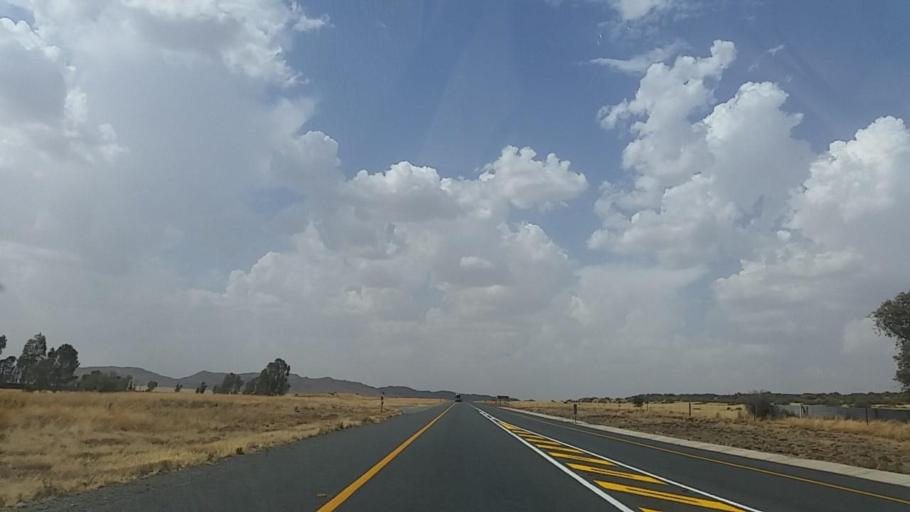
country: ZA
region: Orange Free State
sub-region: Xhariep District Municipality
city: Trompsburg
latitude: -30.4340
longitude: 25.6293
